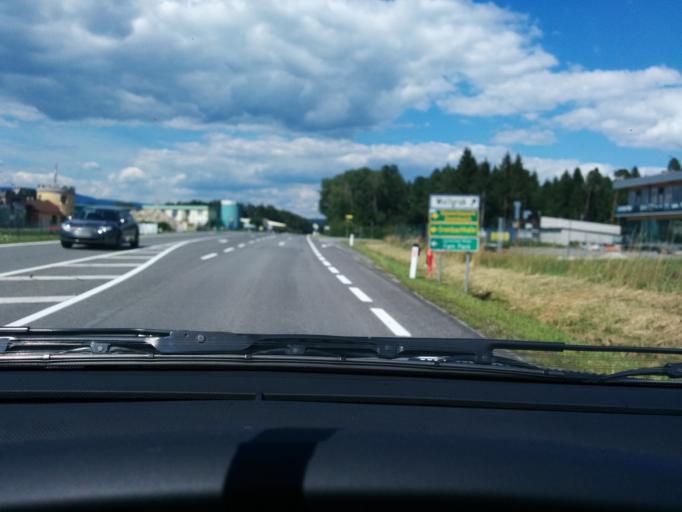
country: AT
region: Styria
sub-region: Politischer Bezirk Hartberg-Fuerstenfeld
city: Hartberg
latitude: 47.3146
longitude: 15.9821
